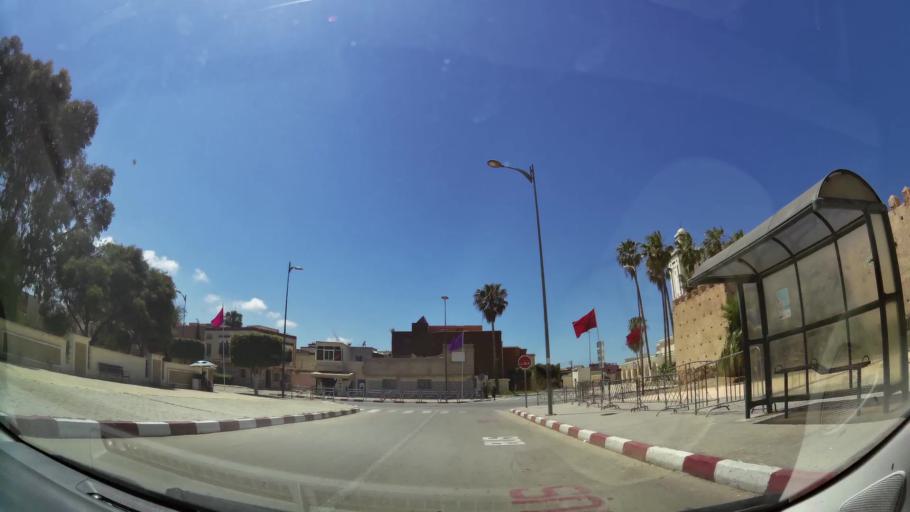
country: MA
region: Oriental
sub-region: Berkane-Taourirt
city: Madagh
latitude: 35.0790
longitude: -2.2156
